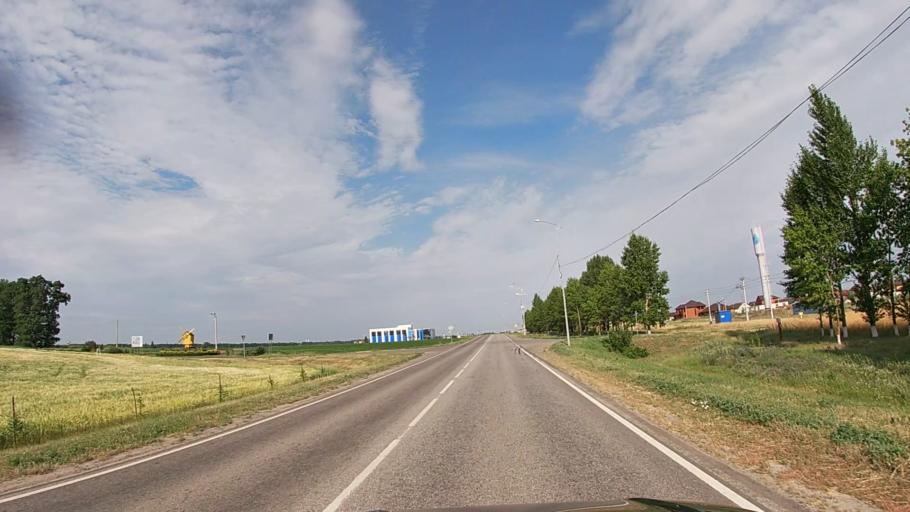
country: RU
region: Belgorod
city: Krasnaya Yaruga
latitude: 50.7959
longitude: 35.6971
